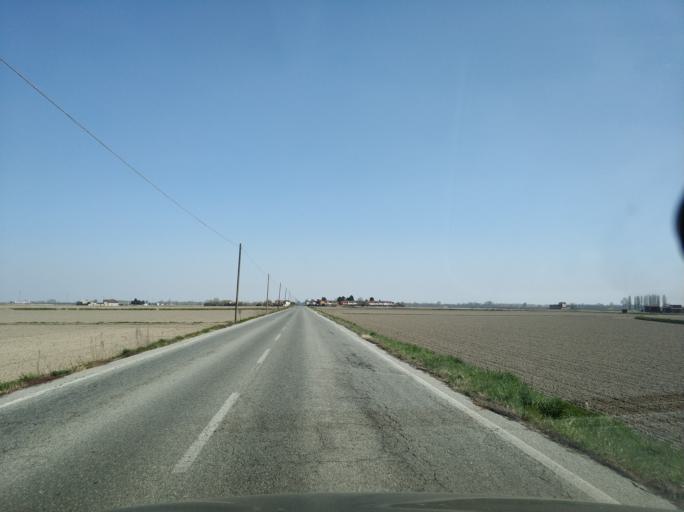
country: IT
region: Piedmont
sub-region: Provincia di Novara
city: Vinzaglio
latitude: 45.3192
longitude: 8.4861
